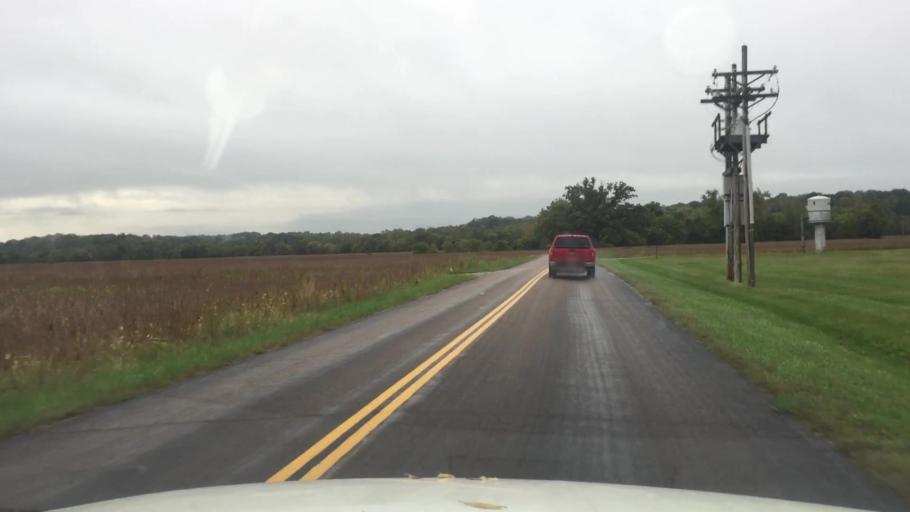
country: US
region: Missouri
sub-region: Boone County
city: Columbia
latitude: 38.8962
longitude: -92.4646
